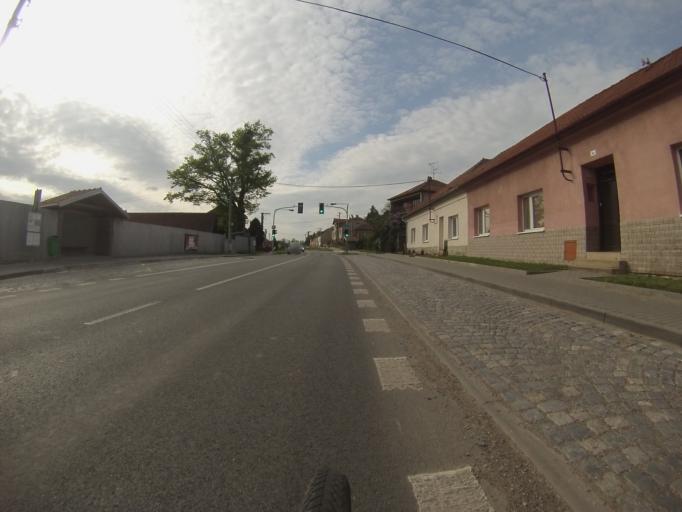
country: CZ
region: South Moravian
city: Tisnov
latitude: 49.3282
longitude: 16.4421
